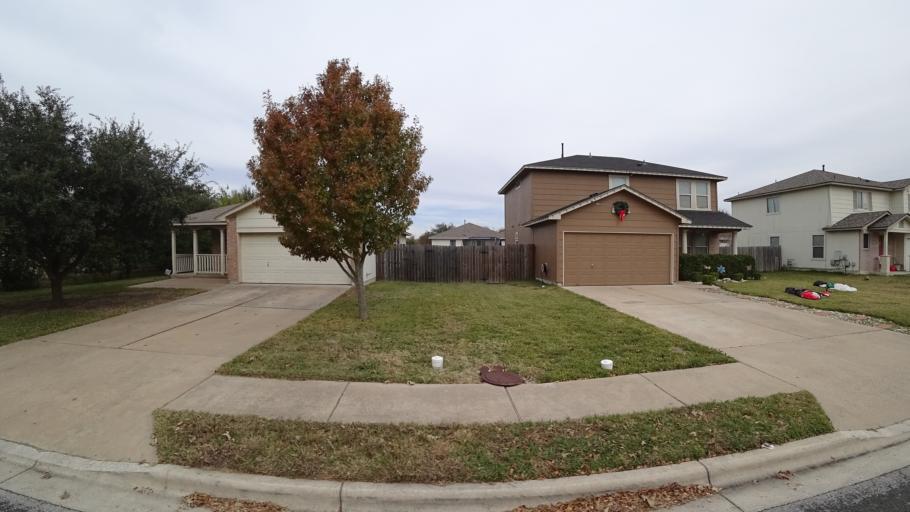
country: US
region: Texas
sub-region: Travis County
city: Onion Creek
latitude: 30.1536
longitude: -97.7403
